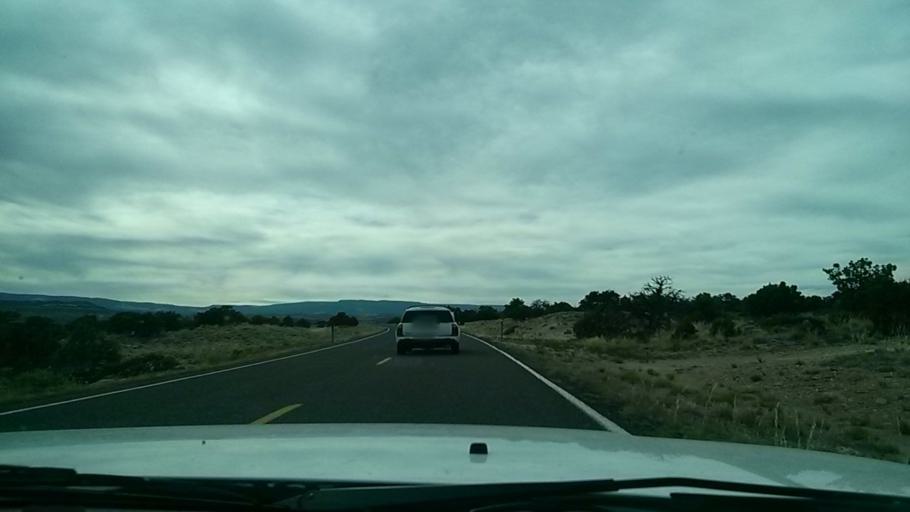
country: US
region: Utah
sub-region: Wayne County
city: Loa
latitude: 37.7367
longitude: -111.5453
